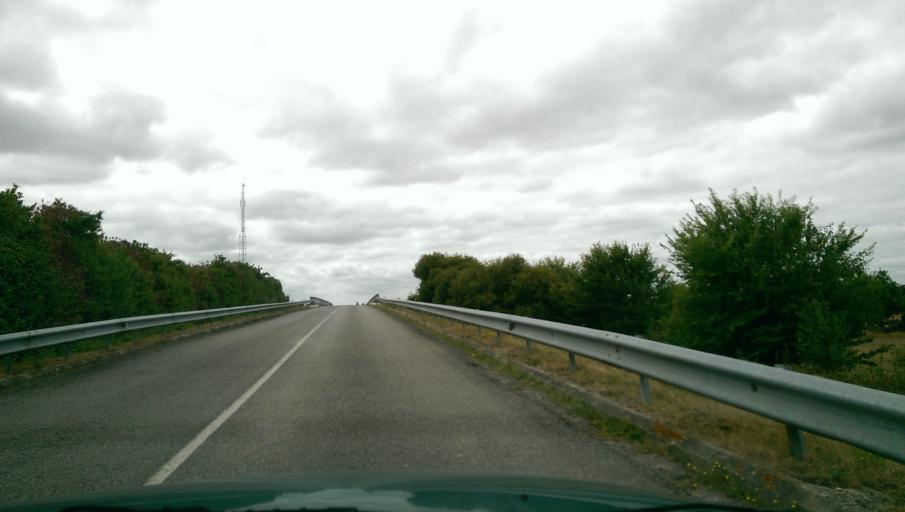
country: FR
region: Pays de la Loire
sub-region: Departement de la Loire-Atlantique
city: La Planche
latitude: 47.0303
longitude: -1.4042
